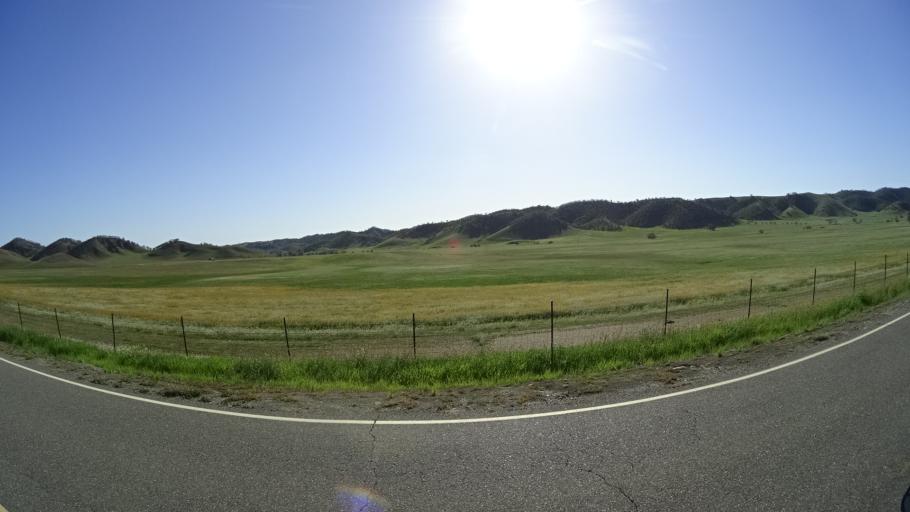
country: US
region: California
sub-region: Tehama County
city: Rancho Tehama Reserve
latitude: 39.7569
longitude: -122.5256
